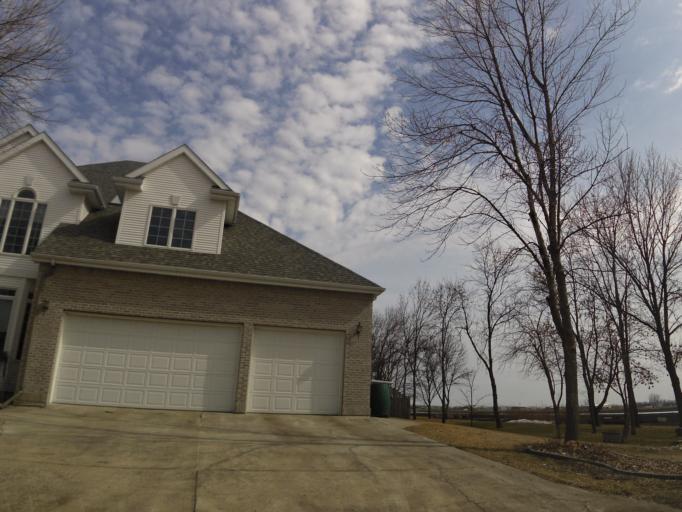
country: US
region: North Dakota
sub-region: Walsh County
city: Grafton
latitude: 48.4045
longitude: -97.4145
